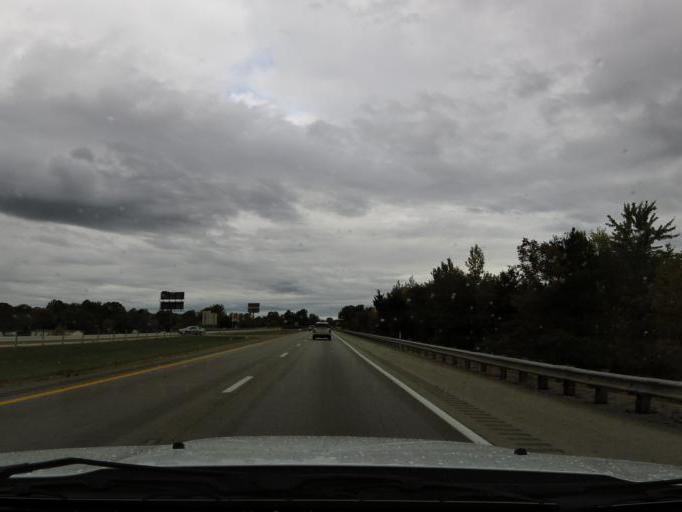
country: US
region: Kentucky
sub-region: Laurel County
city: London
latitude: 37.1658
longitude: -84.1200
